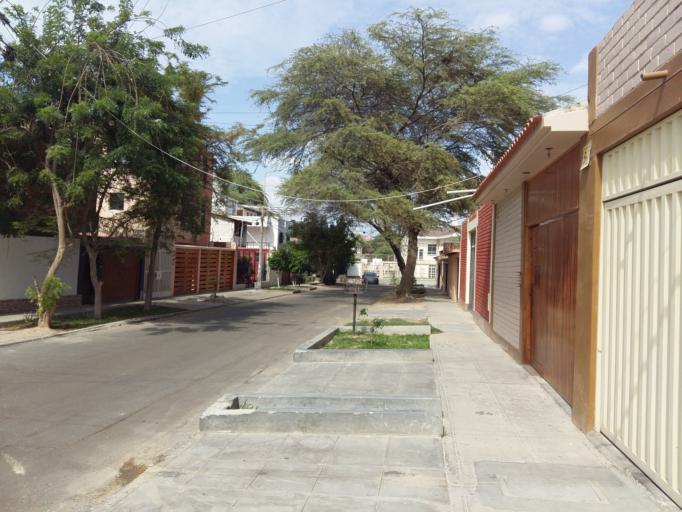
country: PE
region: Piura
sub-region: Provincia de Piura
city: Piura
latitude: -5.1892
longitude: -80.6220
